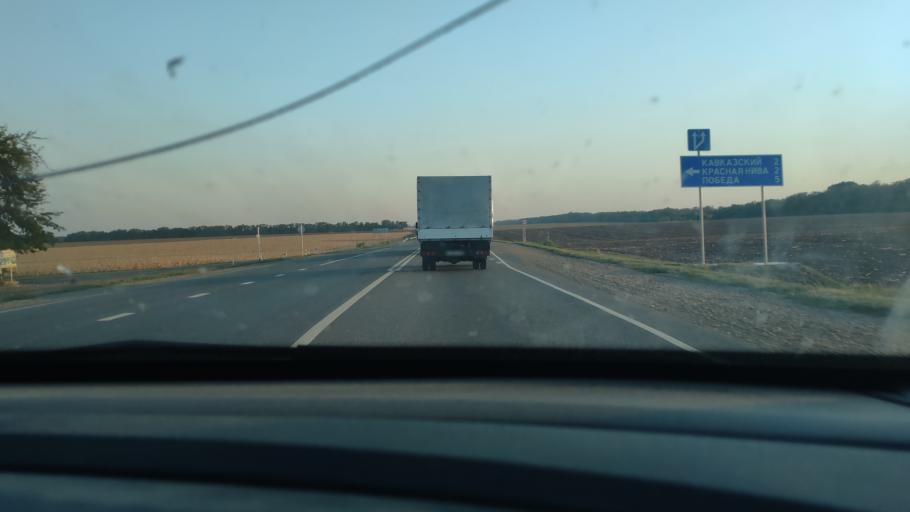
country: RU
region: Krasnodarskiy
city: Bryukhovetskaya
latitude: 45.7438
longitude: 38.9865
